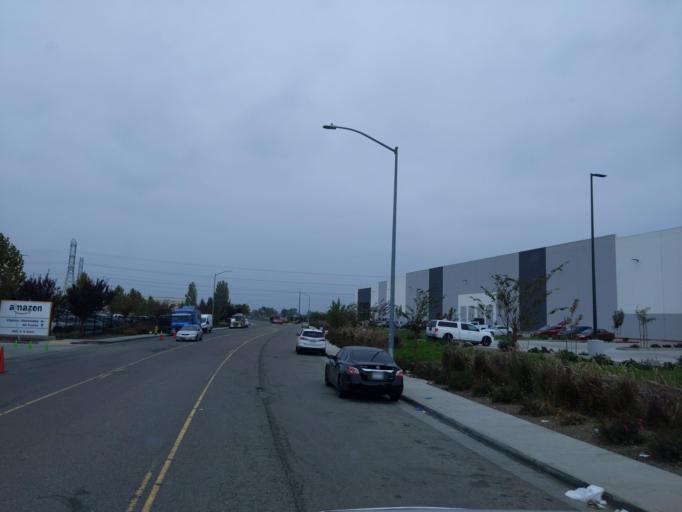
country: US
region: California
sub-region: San Joaquin County
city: Kennedy
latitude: 37.9145
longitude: -121.2479
